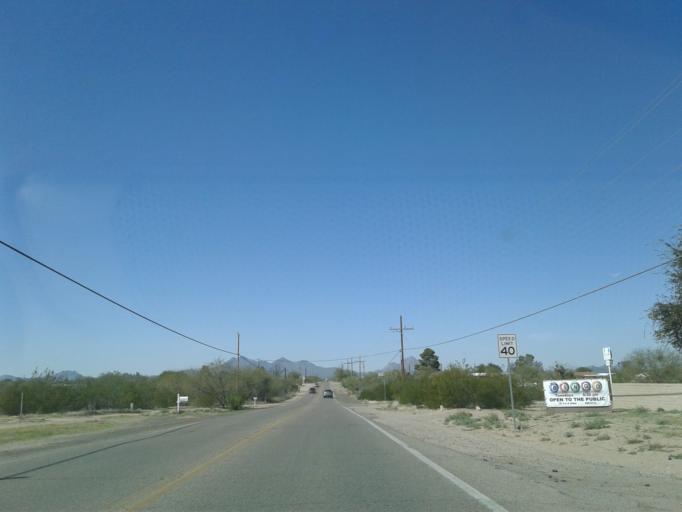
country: US
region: Arizona
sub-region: Pima County
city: Avra Valley
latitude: 32.4294
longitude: -111.3054
